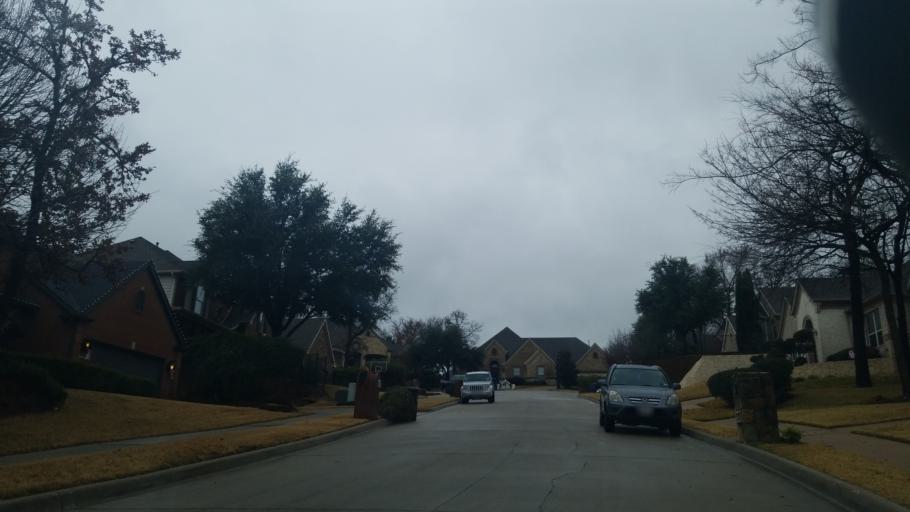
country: US
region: Texas
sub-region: Denton County
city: Corinth
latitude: 33.1463
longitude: -97.0880
